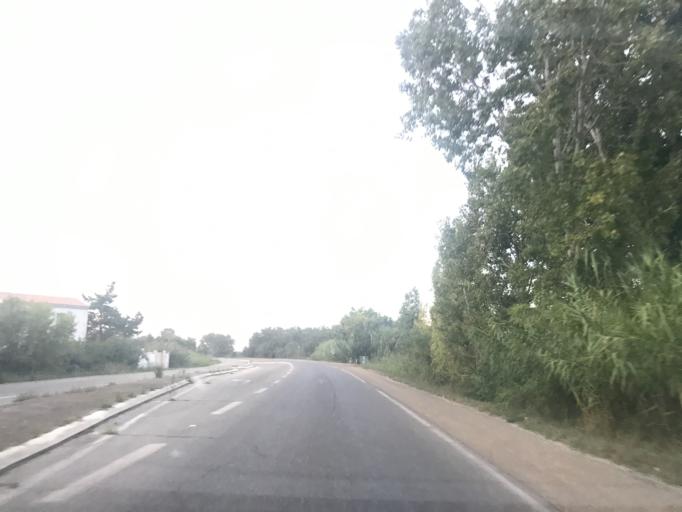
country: FR
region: Provence-Alpes-Cote d'Azur
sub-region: Departement des Bouches-du-Rhone
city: Saintes-Maries-de-la-Mer
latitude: 43.5260
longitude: 4.4007
